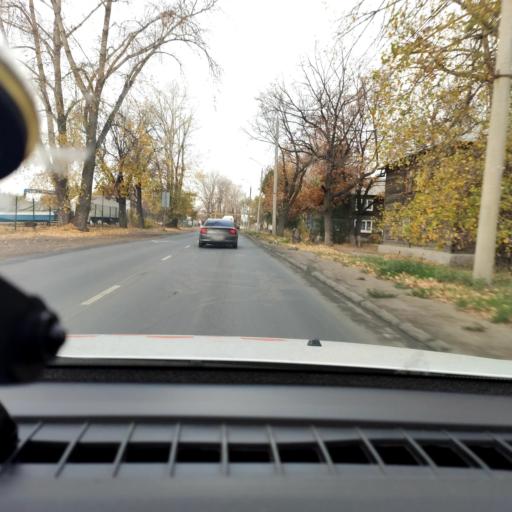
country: RU
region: Samara
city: Rozhdestveno
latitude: 53.1432
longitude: 50.0397
